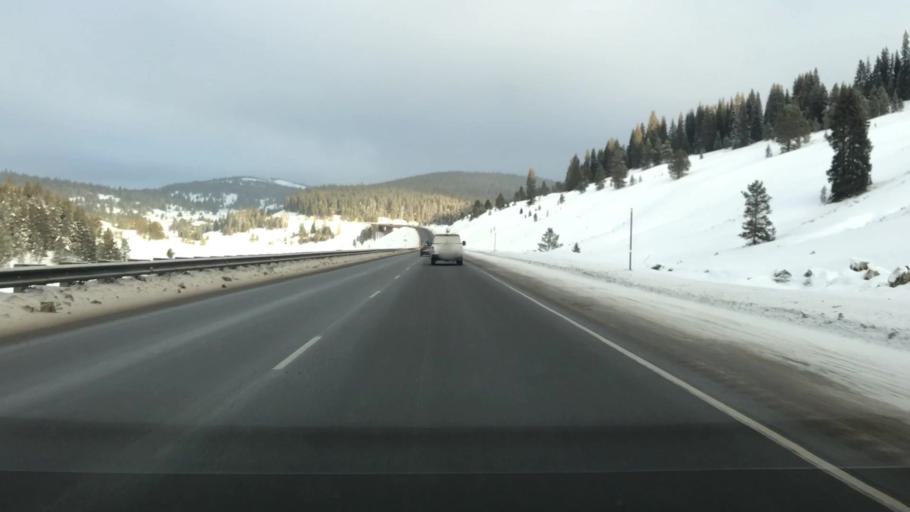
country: US
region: Colorado
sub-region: Summit County
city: Frisco
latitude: 39.5090
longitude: -106.2018
